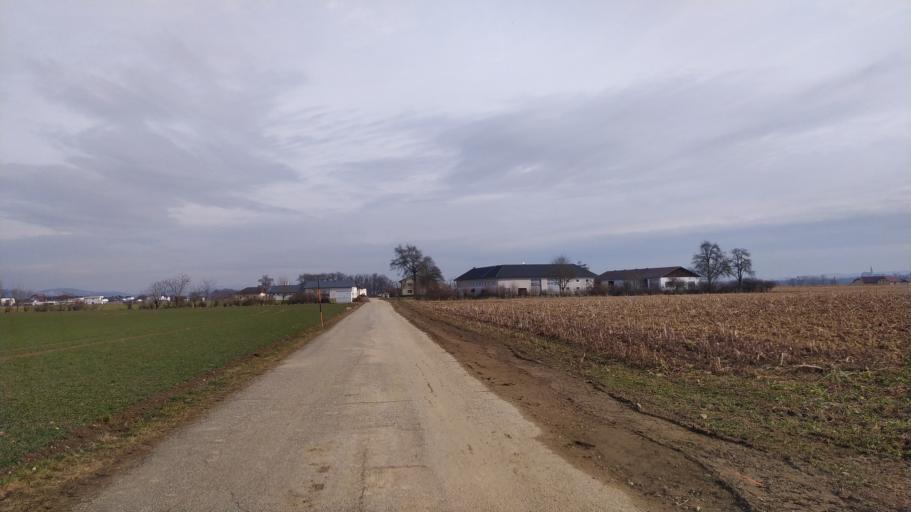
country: AT
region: Upper Austria
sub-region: Politischer Bezirk Perg
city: Perg
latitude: 48.1922
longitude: 14.6717
